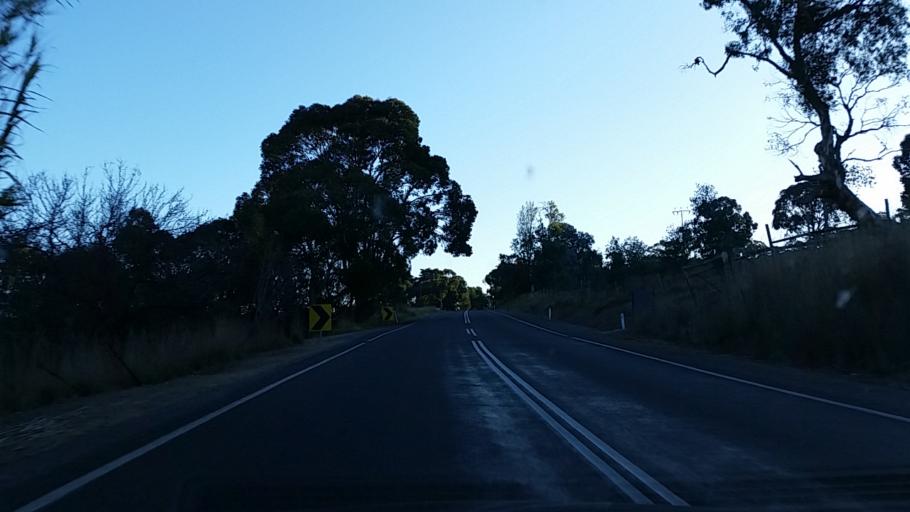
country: AU
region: South Australia
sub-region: Alexandrina
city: Mount Compass
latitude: -35.3470
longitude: 138.6462
